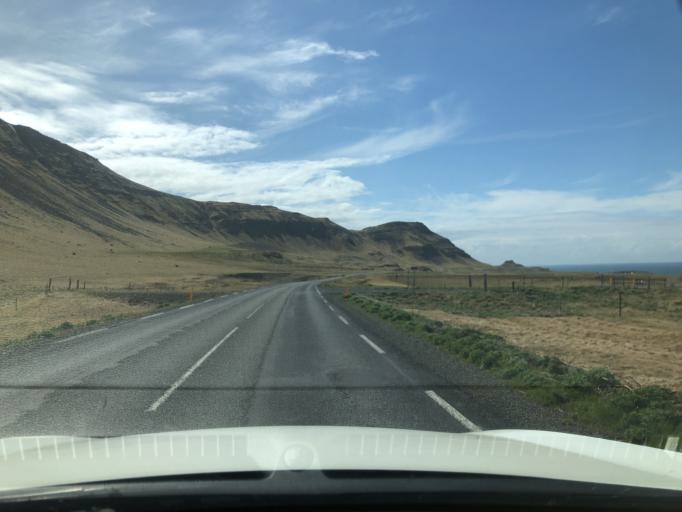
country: IS
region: Capital Region
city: Mosfellsbaer
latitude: 64.2935
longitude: -21.7955
